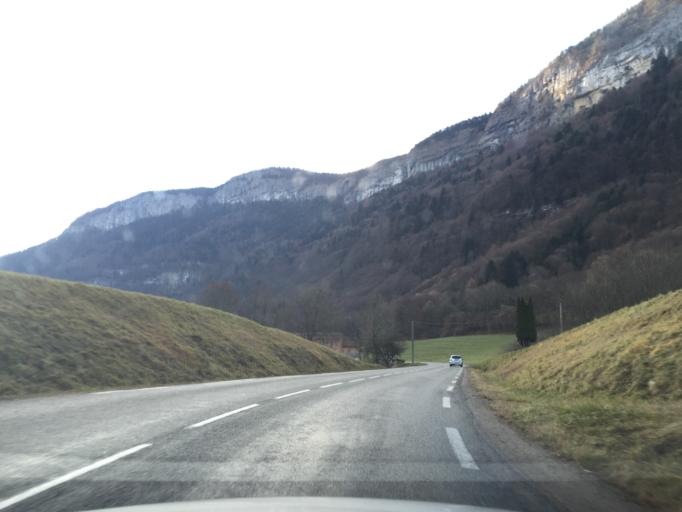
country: FR
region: Rhone-Alpes
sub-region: Departement de la Haute-Savoie
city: Gruffy
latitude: 45.7587
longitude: 6.0580
